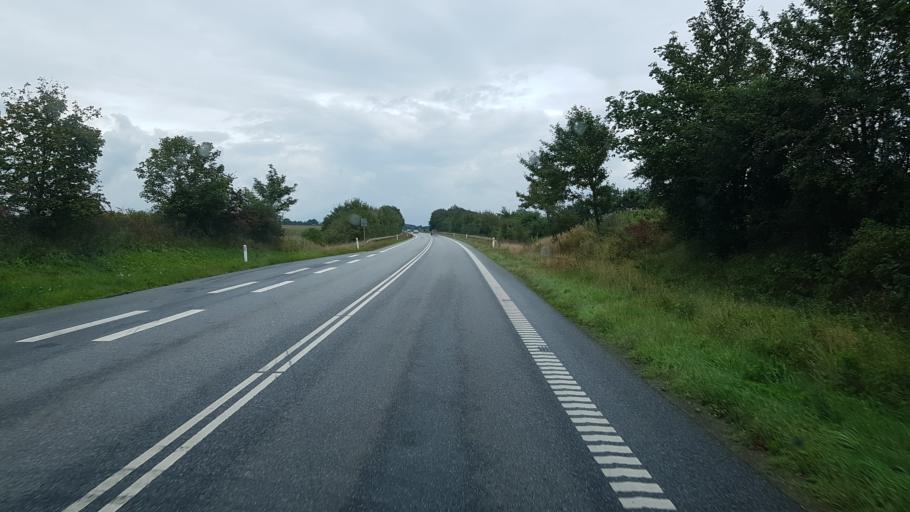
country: DK
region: Central Jutland
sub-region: Horsens Kommune
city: Braedstrup
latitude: 55.9231
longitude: 9.6812
